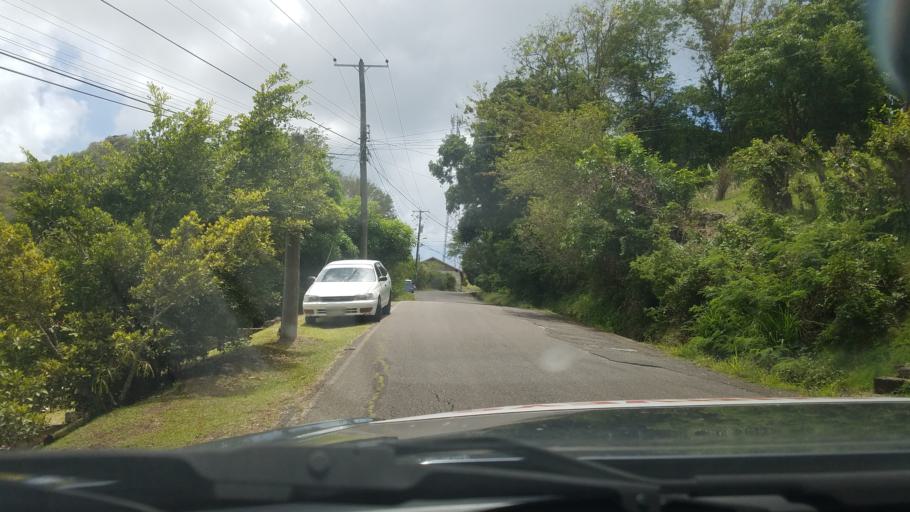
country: LC
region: Gros-Islet
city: Gros Islet
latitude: 14.0572
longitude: -60.9372
